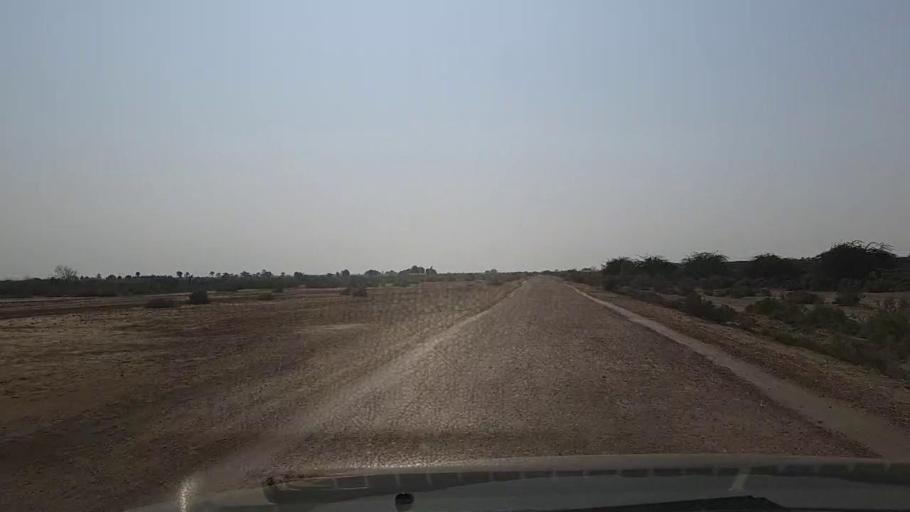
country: PK
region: Sindh
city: Mirpur Sakro
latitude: 24.3865
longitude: 67.6638
